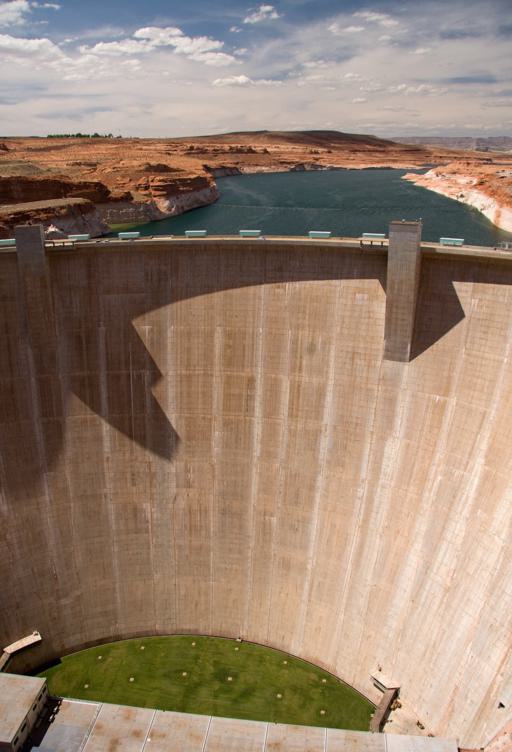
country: US
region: Arizona
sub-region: Coconino County
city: Page
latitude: 36.9359
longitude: -111.4828
